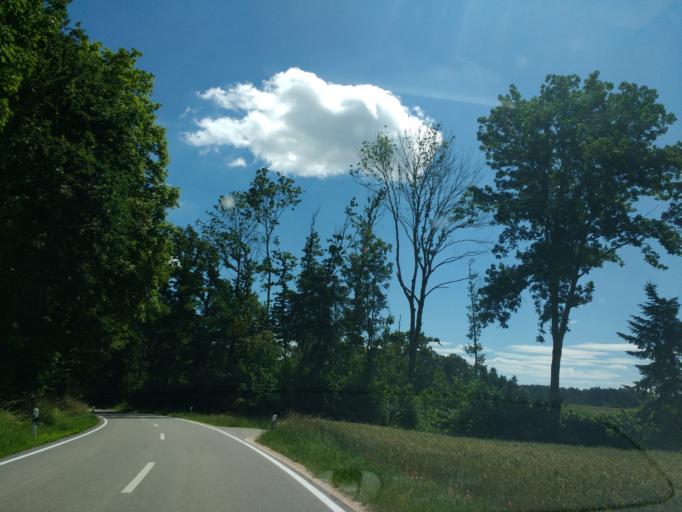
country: DE
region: Bavaria
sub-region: Upper Bavaria
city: Engelsberg
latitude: 48.1237
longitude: 12.5074
